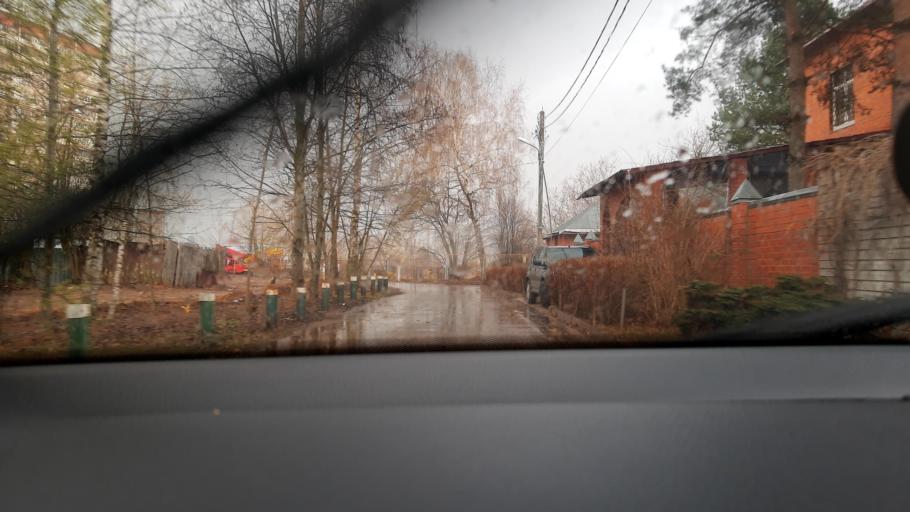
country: RU
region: Moskovskaya
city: Pirogovskiy
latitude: 55.9815
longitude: 37.7352
